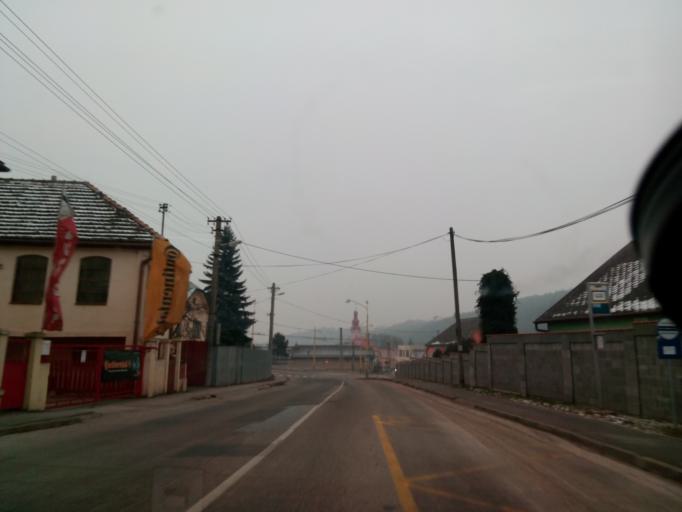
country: SK
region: Kosicky
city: Kosice
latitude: 48.7102
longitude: 21.2040
